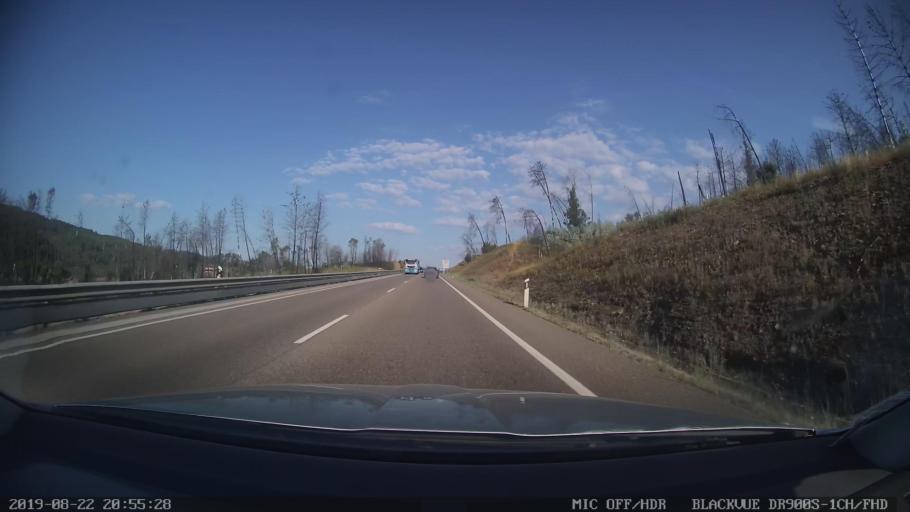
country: PT
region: Castelo Branco
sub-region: Serta
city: Serta
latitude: 39.7805
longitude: -8.0339
